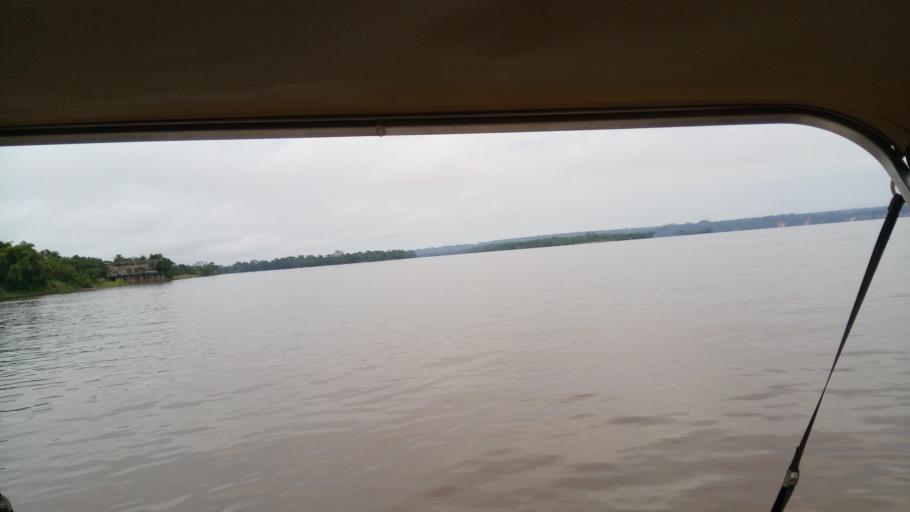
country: CD
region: Eastern Province
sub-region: Sous-Region de la Tshopo
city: Yangambi
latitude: 0.7139
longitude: 24.5622
